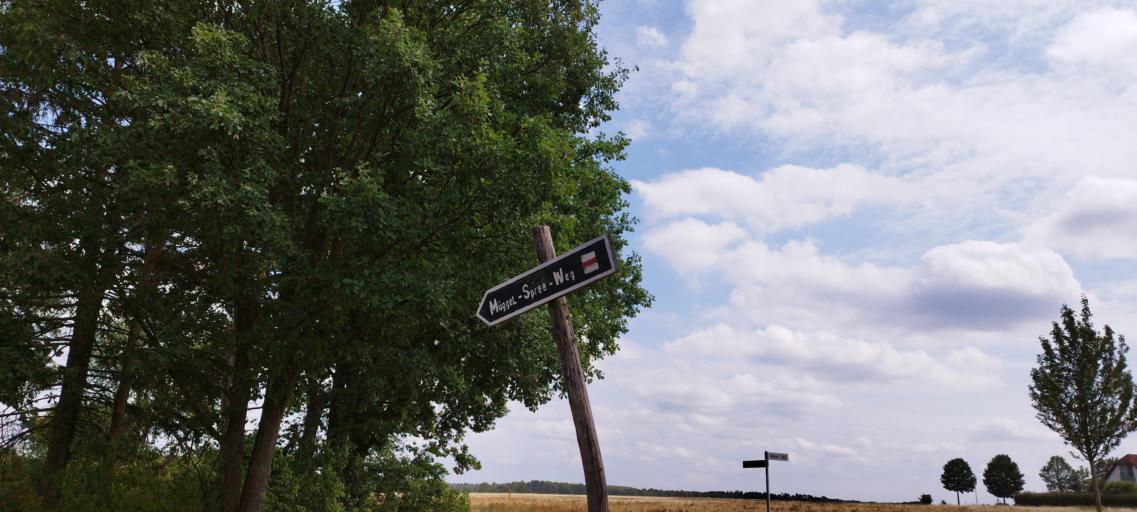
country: DE
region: Brandenburg
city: Schoneiche
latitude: 52.4836
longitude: 13.7178
